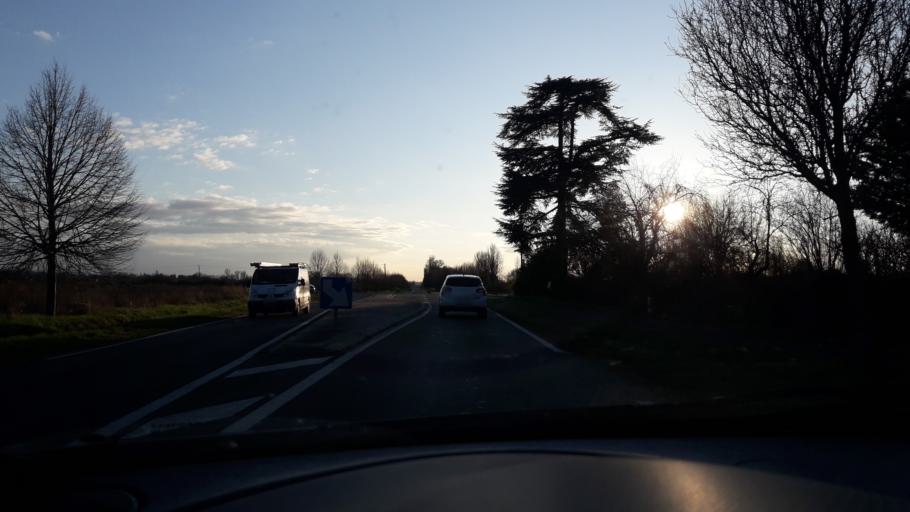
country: FR
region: Midi-Pyrenees
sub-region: Departement de la Haute-Garonne
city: Levignac
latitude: 43.6535
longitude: 1.1756
